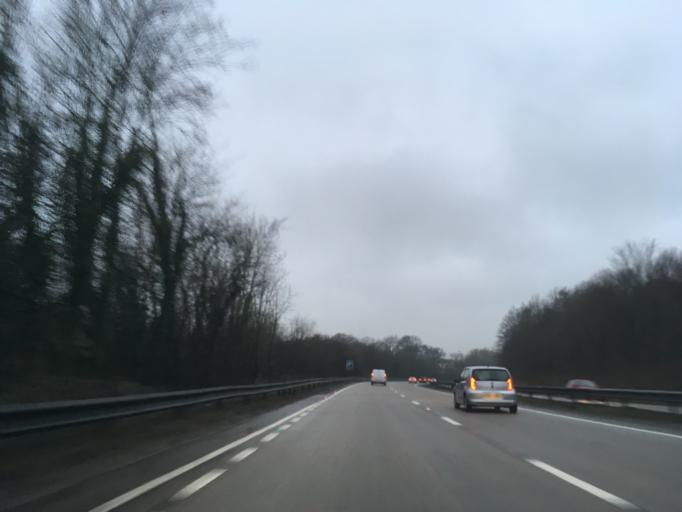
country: GB
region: Wales
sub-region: Cardiff
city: Radyr
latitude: 51.4704
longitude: -3.2767
